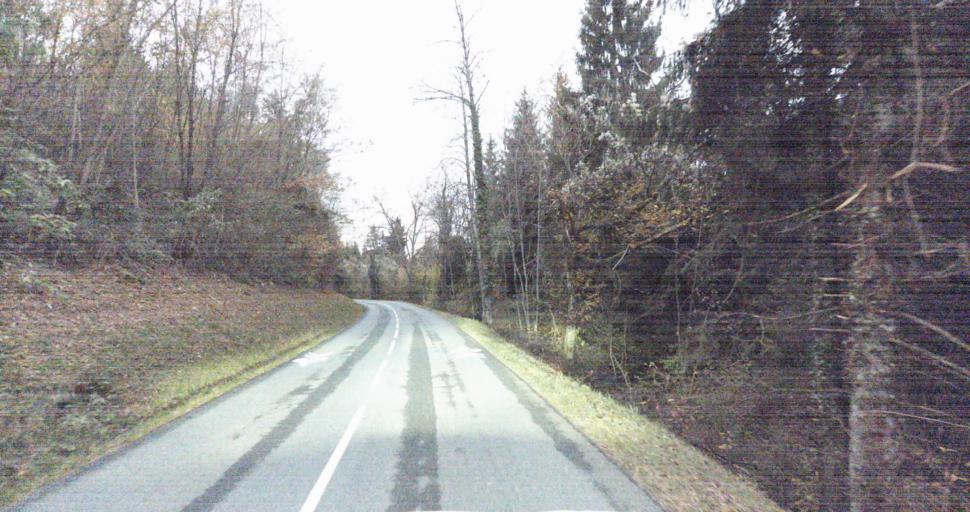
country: FR
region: Rhone-Alpes
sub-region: Departement de la Haute-Savoie
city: Saint-Jorioz
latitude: 45.8346
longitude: 6.1424
